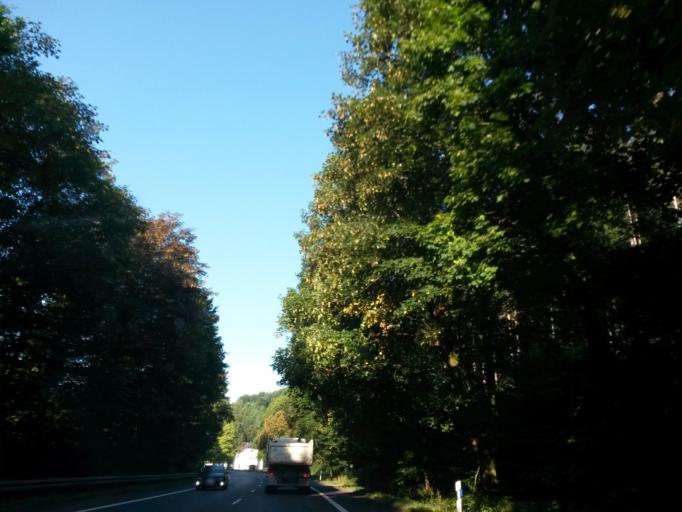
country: DE
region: North Rhine-Westphalia
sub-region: Regierungsbezirk Koln
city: Engelskirchen
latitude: 51.0198
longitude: 7.4447
